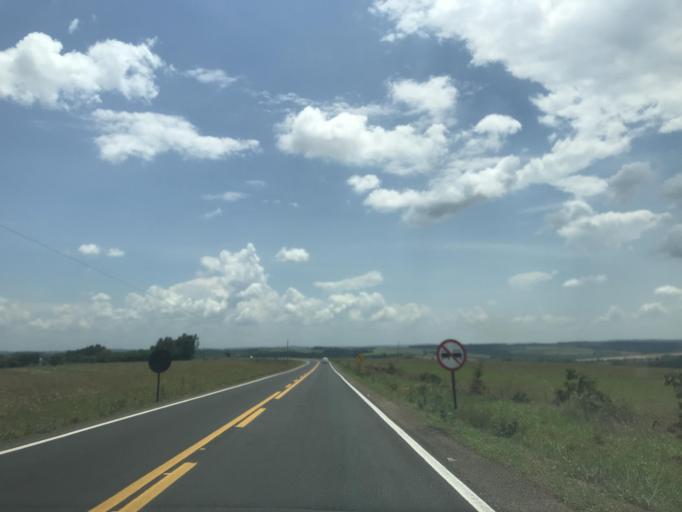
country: BR
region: Goias
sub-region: Bela Vista De Goias
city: Bela Vista de Goias
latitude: -17.1027
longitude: -48.6627
